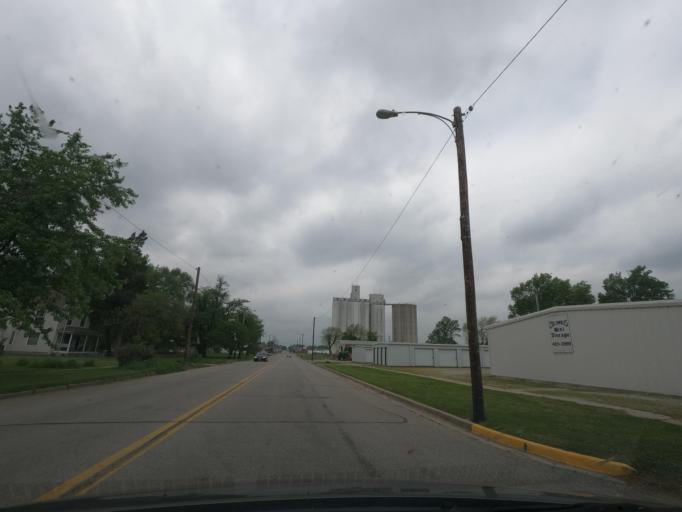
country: US
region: Kansas
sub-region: Cherokee County
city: Columbus
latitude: 37.1709
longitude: -94.8345
